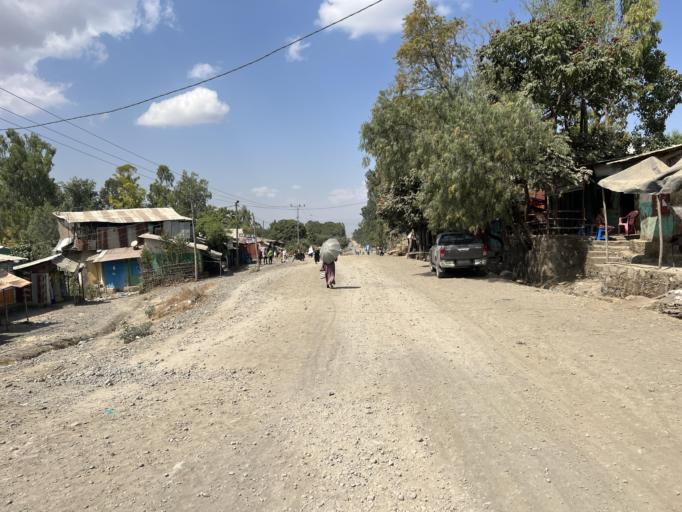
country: ET
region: Oromiya
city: Fiche
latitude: 10.0604
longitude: 38.9936
